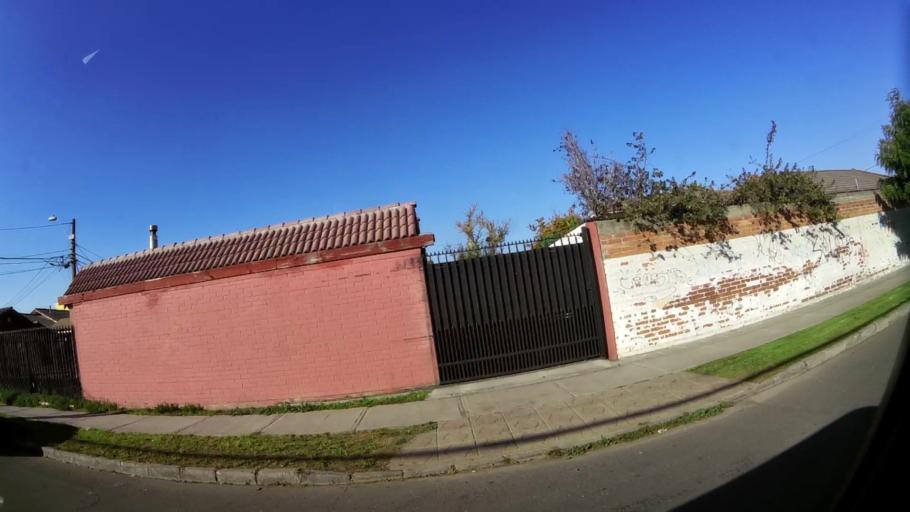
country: CL
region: Santiago Metropolitan
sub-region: Provincia de Santiago
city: Lo Prado
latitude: -33.4860
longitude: -70.7581
